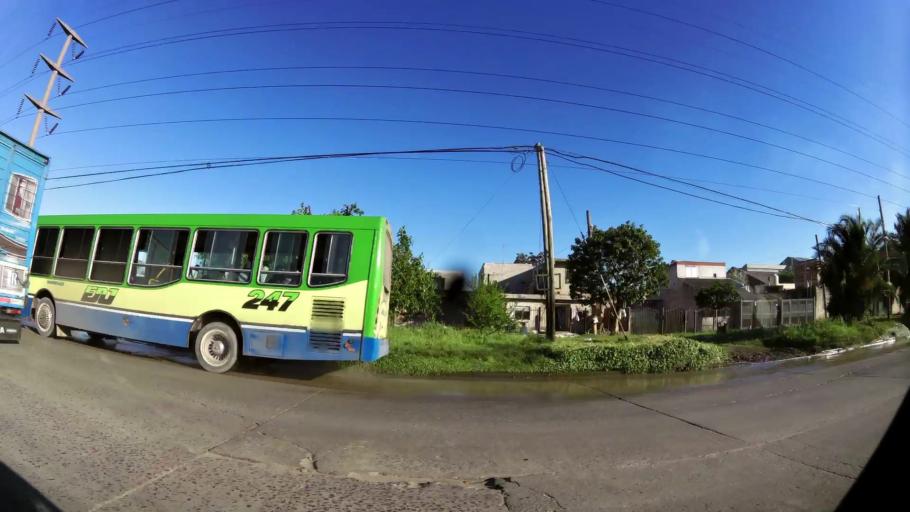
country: AR
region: Buenos Aires
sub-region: Partido de Almirante Brown
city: Adrogue
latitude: -34.7481
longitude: -58.3339
